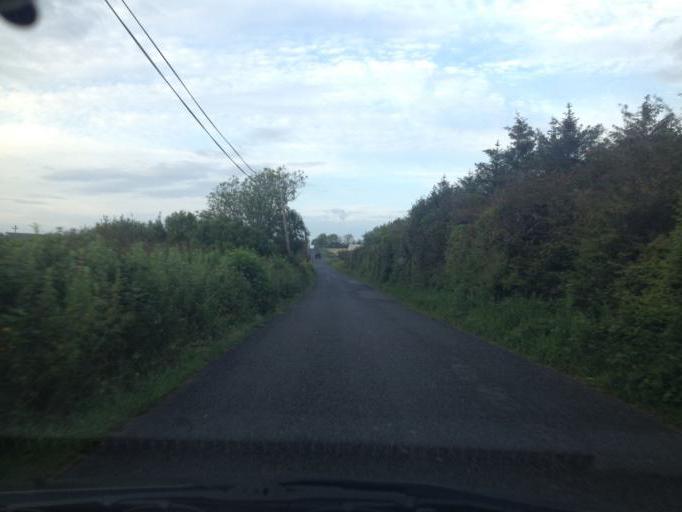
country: IE
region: Connaught
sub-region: Sligo
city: Strandhill
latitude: 54.3761
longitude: -8.5710
